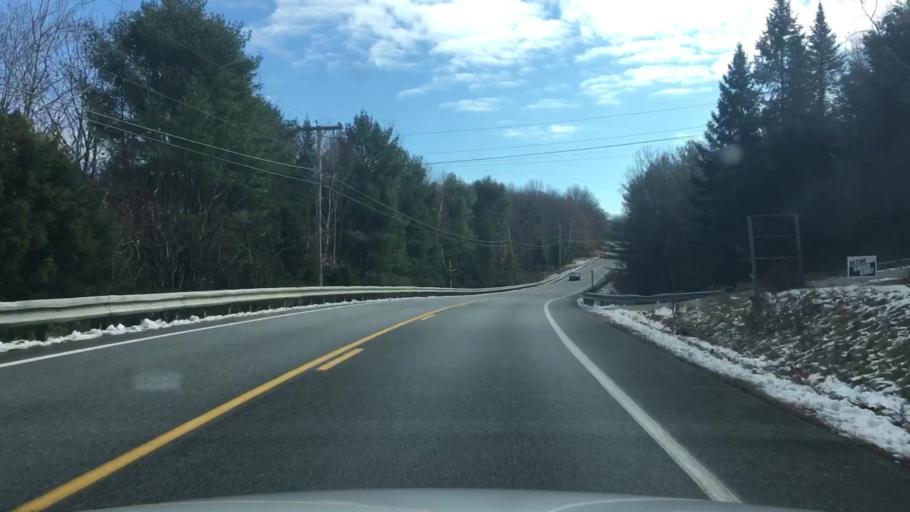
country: US
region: Maine
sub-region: Kennebec County
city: Winthrop
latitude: 44.3322
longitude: -70.0060
